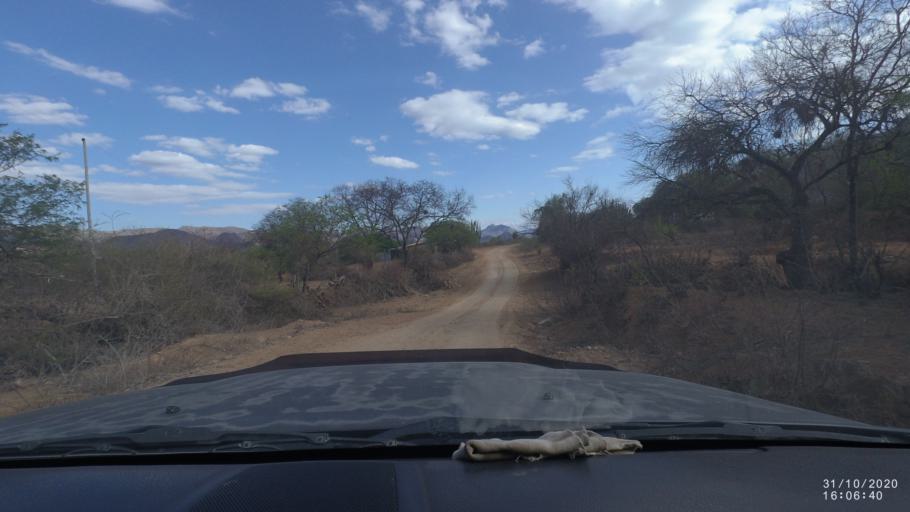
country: BO
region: Chuquisaca
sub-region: Provincia Zudanez
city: Mojocoya
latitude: -18.3746
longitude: -64.6458
